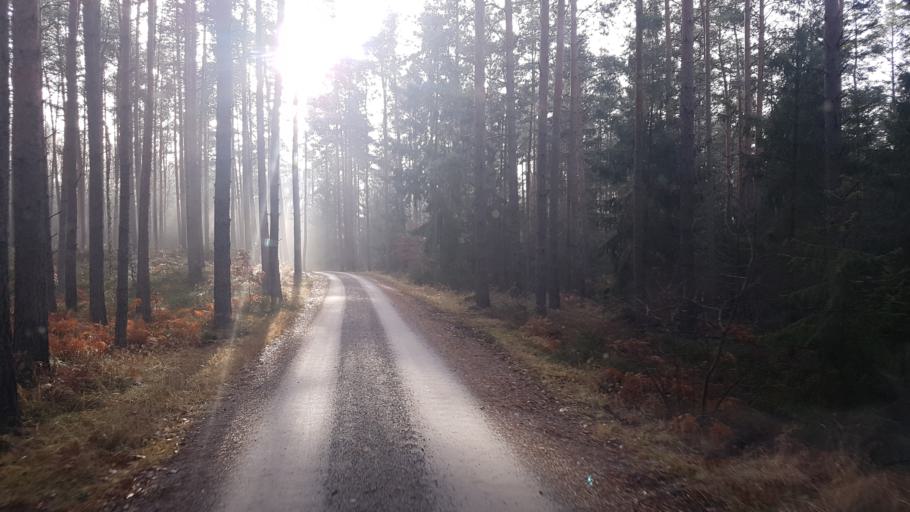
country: DE
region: Brandenburg
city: Schonborn
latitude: 51.6248
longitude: 13.5088
